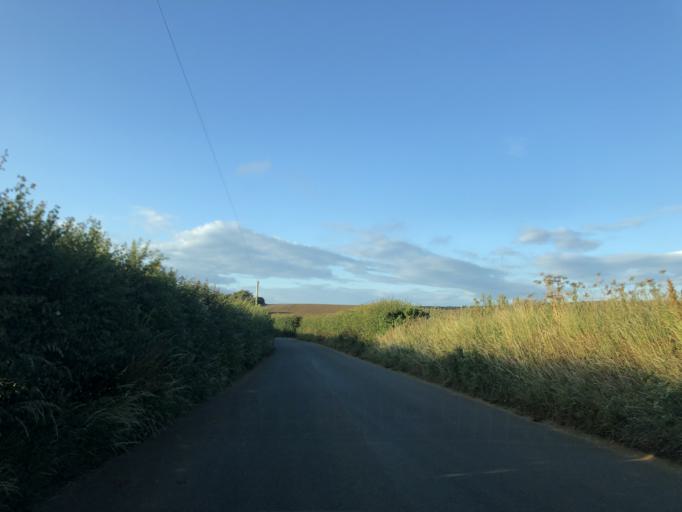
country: GB
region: England
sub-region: Isle of Wight
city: Chale
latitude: 50.6378
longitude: -1.3572
